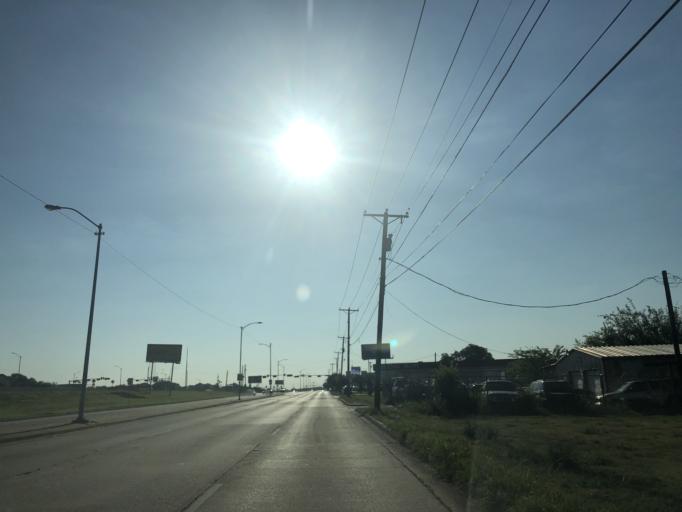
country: US
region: Texas
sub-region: Dallas County
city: Grand Prairie
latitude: 32.7396
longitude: -97.0316
